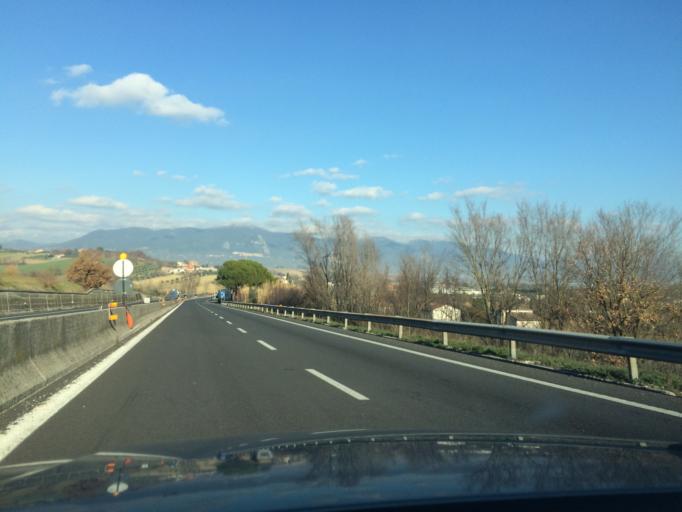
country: IT
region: Umbria
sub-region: Provincia di Terni
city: Narni Scalo
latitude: 42.5452
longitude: 12.5200
